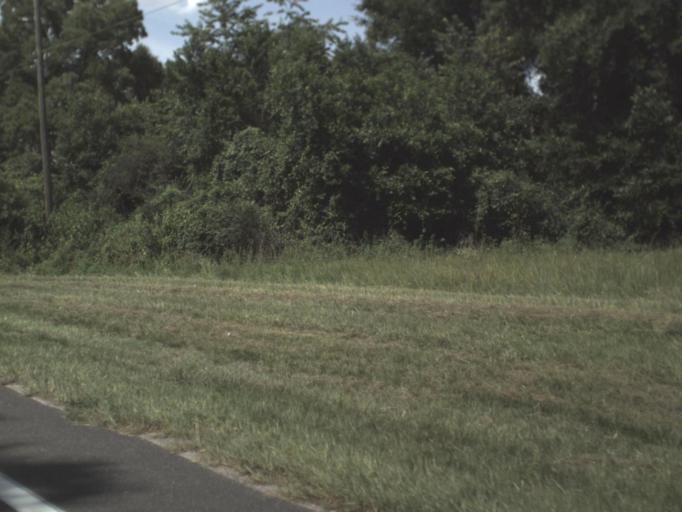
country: US
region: Florida
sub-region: Alachua County
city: High Springs
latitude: 29.9559
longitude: -82.7128
